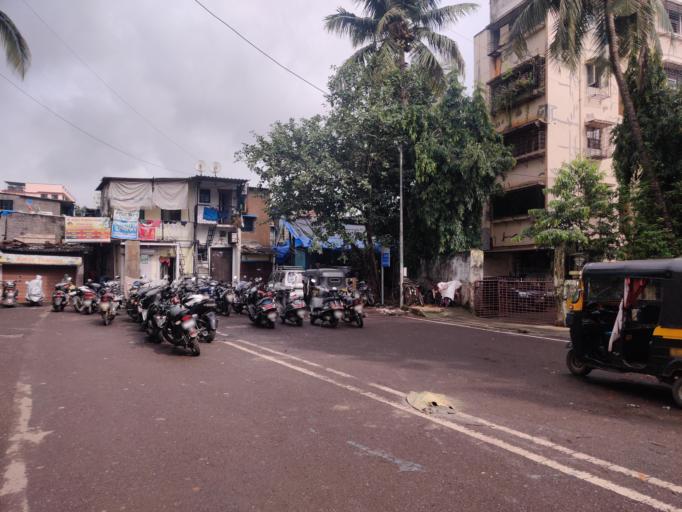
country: IN
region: Maharashtra
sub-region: Mumbai Suburban
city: Borivli
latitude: 19.2442
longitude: 72.8554
